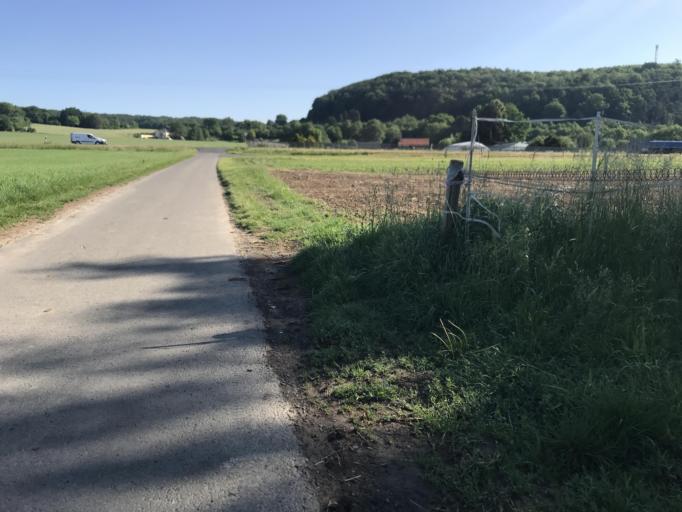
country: DE
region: Hesse
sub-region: Regierungsbezirk Giessen
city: Grossen Buseck
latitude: 50.6131
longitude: 8.7752
